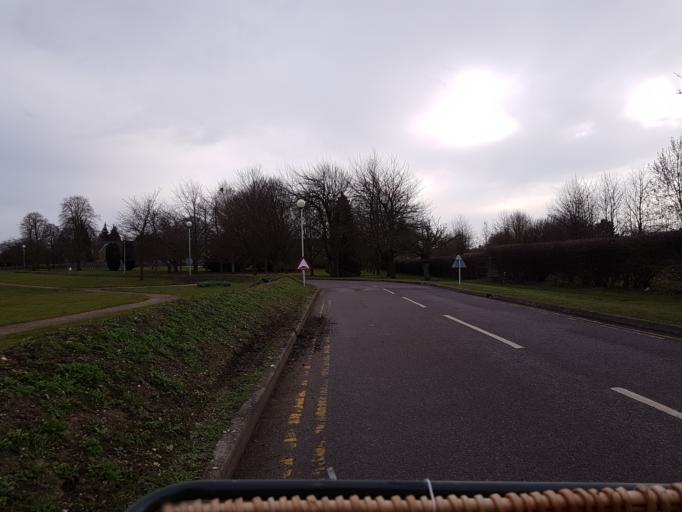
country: GB
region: England
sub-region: Cambridgeshire
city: Fulbourn
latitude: 52.1846
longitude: 0.1858
